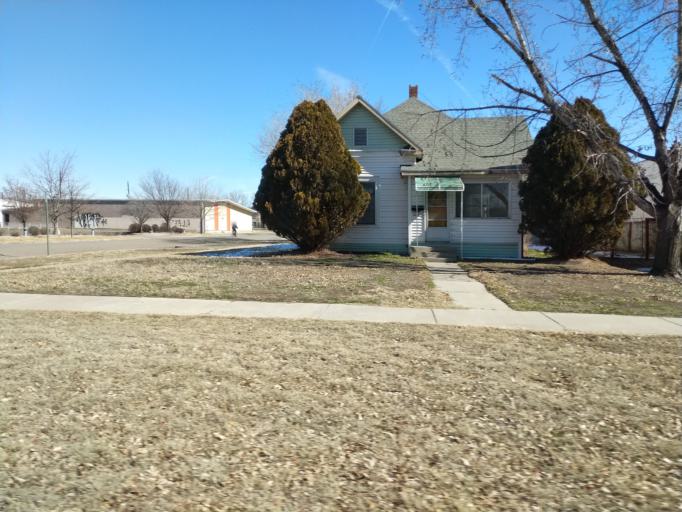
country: US
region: Colorado
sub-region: Mesa County
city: Grand Junction
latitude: 39.0761
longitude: -108.5610
